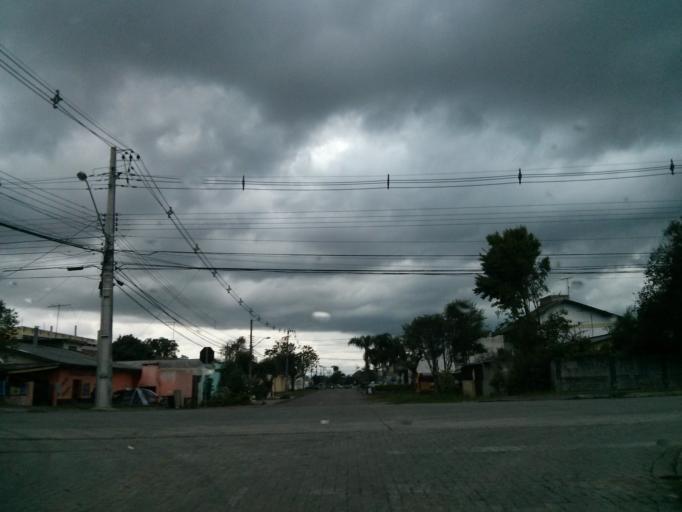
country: BR
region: Parana
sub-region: Sao Jose Dos Pinhais
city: Sao Jose dos Pinhais
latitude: -25.5192
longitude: -49.2277
